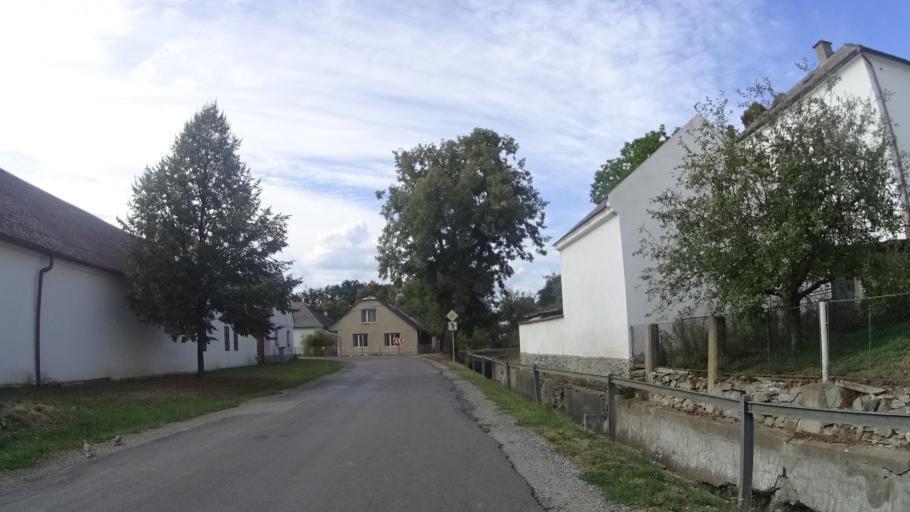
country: CZ
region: Olomoucky
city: Dubicko
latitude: 49.7962
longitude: 16.9635
